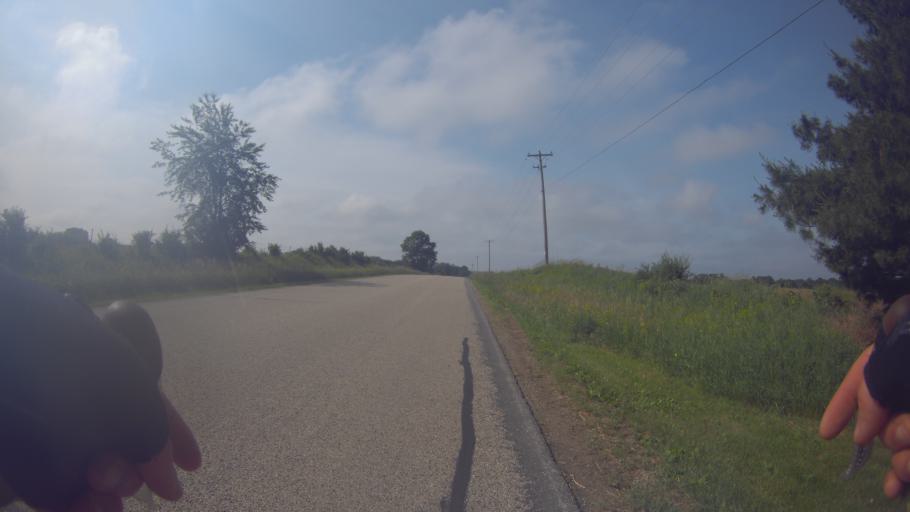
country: US
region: Wisconsin
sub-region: Dane County
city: McFarland
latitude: 42.9963
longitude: -89.2352
